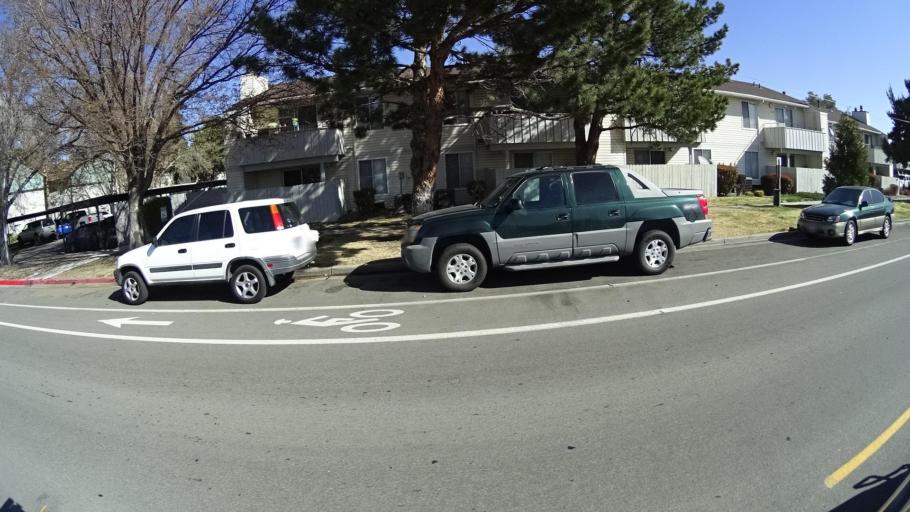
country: US
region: Nevada
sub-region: Washoe County
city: Reno
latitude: 39.4695
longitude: -119.7783
